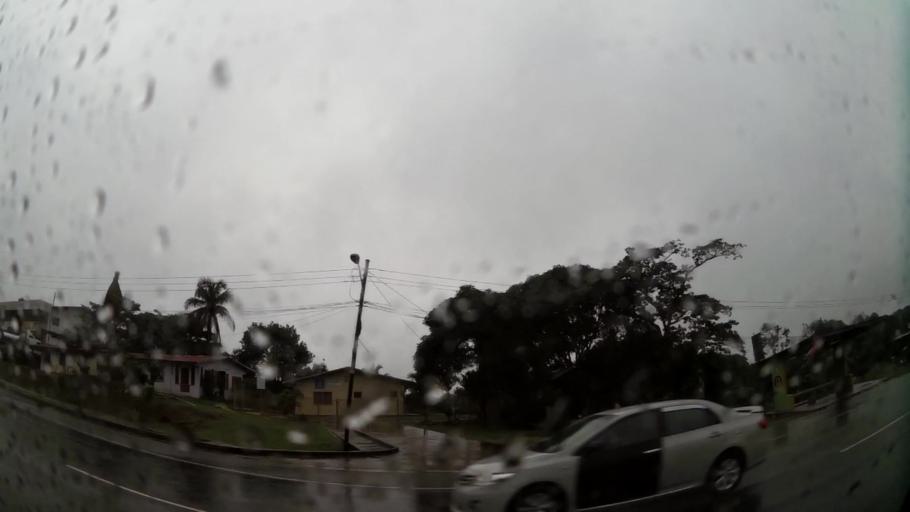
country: PA
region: Colon
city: Santa Rita Arriba
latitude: 9.3177
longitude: -79.7951
